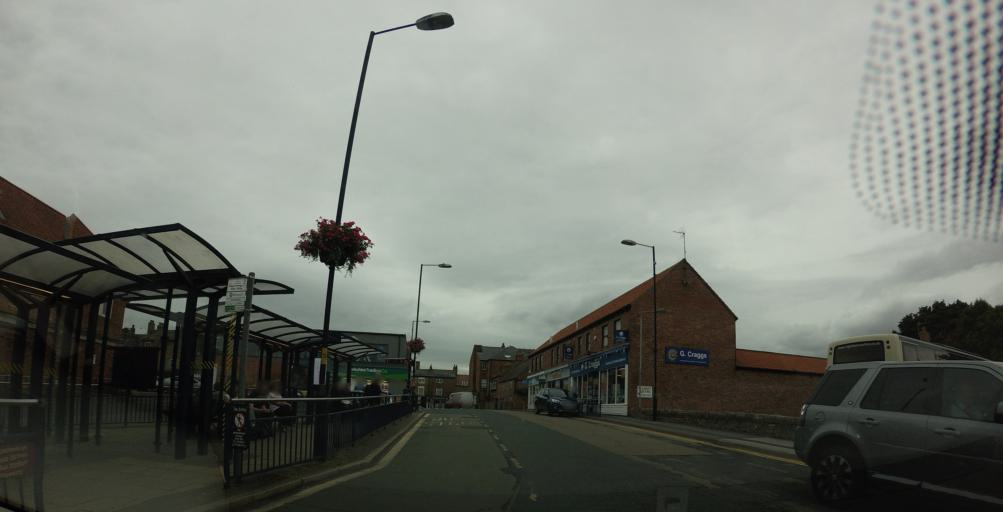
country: GB
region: England
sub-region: North Yorkshire
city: Ripon
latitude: 54.1370
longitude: -1.5218
